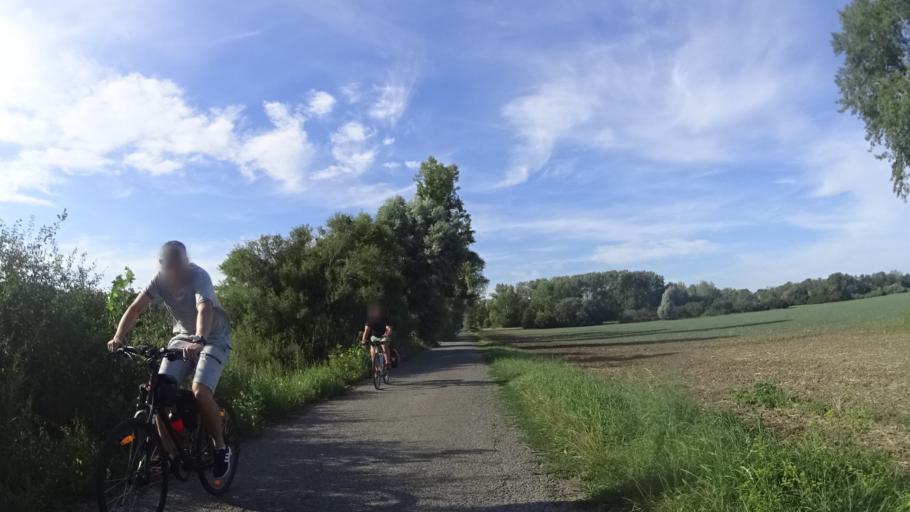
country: AT
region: Lower Austria
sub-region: Politischer Bezirk Ganserndorf
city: Drosing
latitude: 48.5926
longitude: 16.9503
